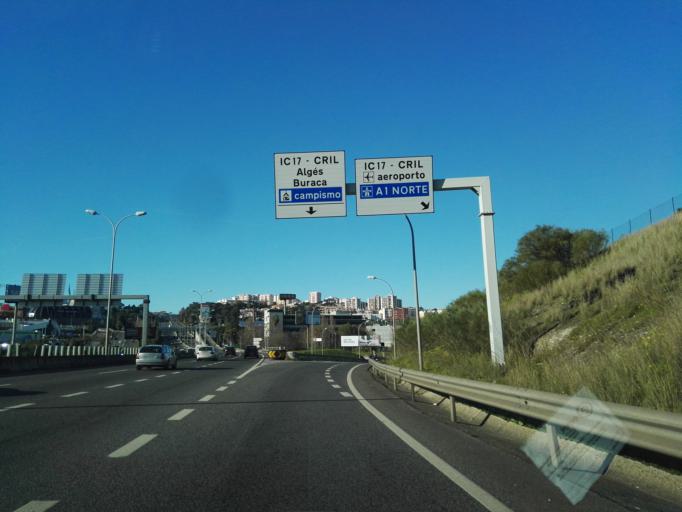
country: PT
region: Lisbon
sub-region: Oeiras
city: Alges
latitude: 38.7243
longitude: -9.2125
